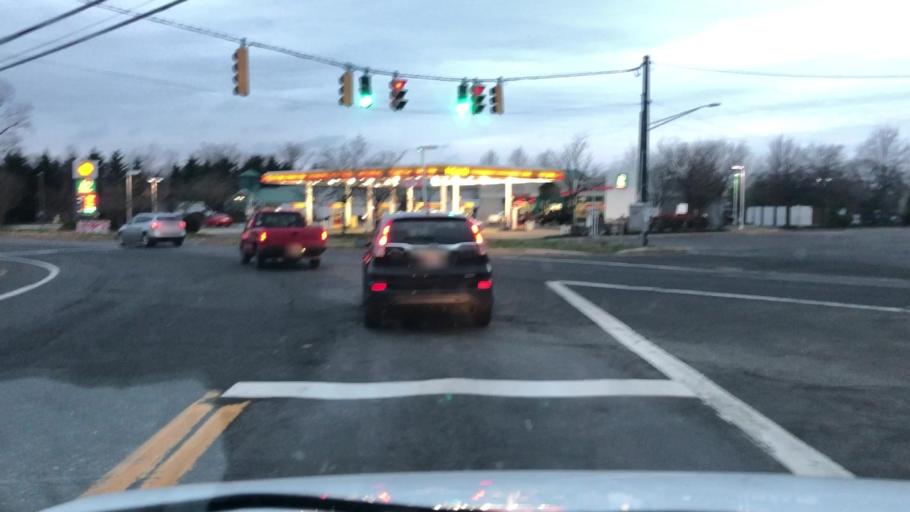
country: US
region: Maryland
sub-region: Prince George's County
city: Marlboro Meadows
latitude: 38.8115
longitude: -76.7017
